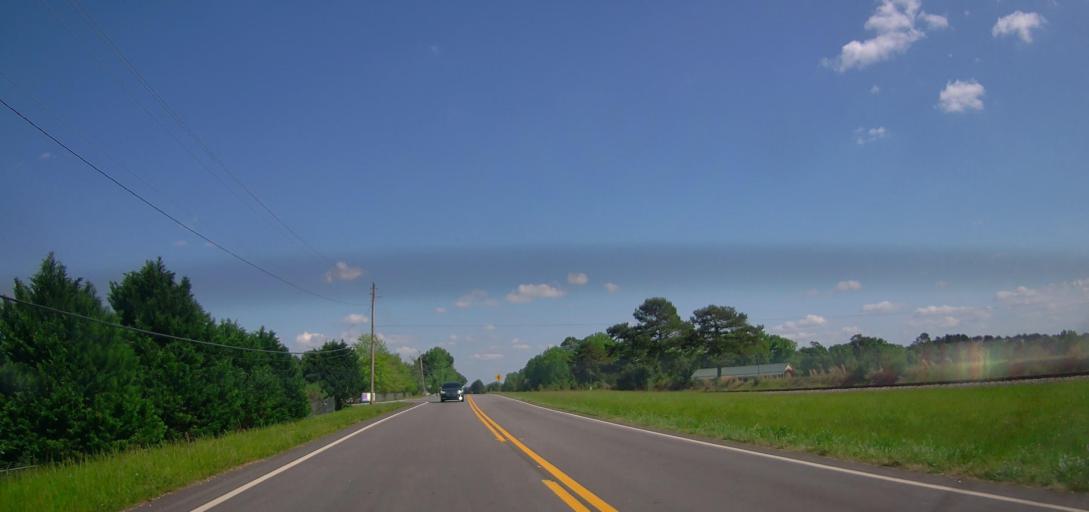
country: US
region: Georgia
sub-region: Morgan County
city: Madison
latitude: 33.6110
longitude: -83.4357
